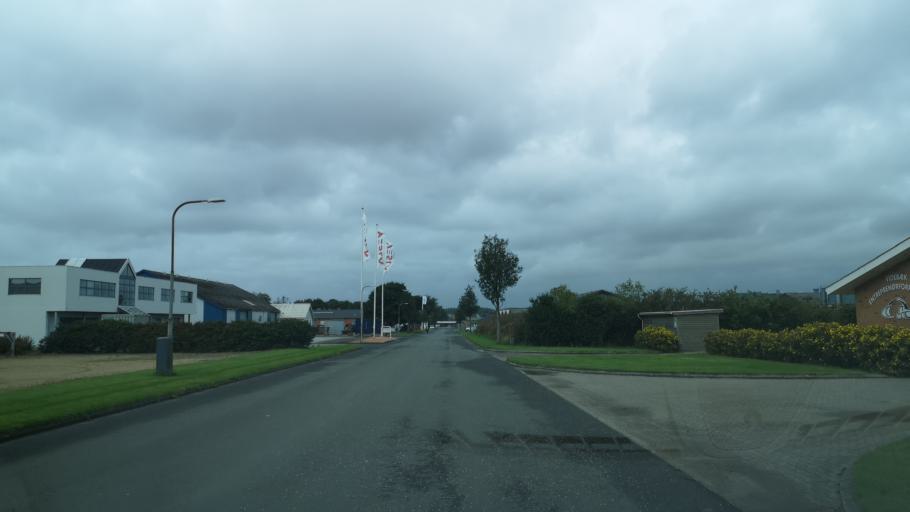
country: DK
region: Central Jutland
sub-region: Ringkobing-Skjern Kommune
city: Videbaek
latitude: 56.0896
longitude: 8.6455
